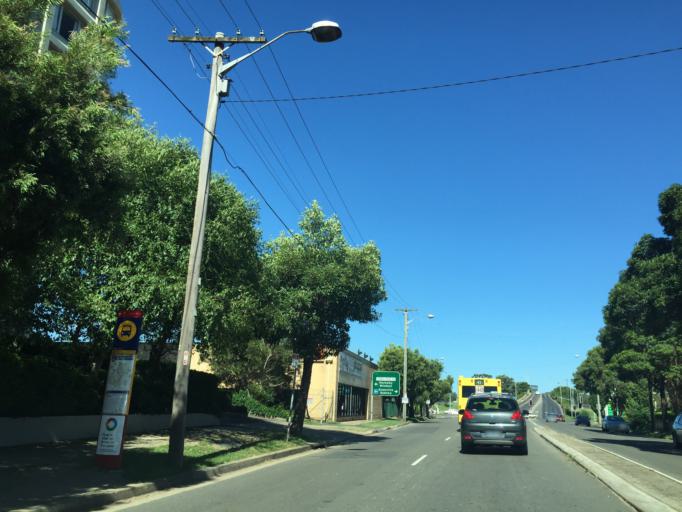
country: AU
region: New South Wales
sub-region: Parramatta
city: Harris Park
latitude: -33.8190
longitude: 151.0201
